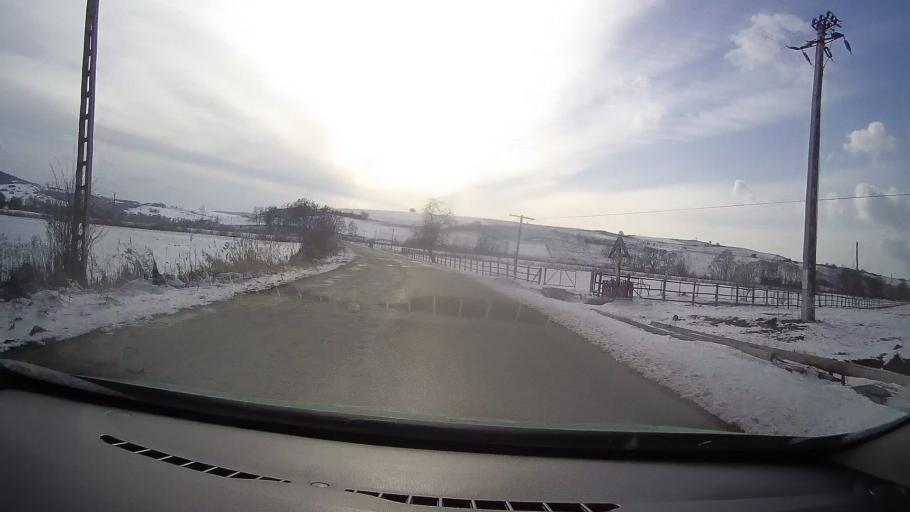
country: RO
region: Sibiu
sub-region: Comuna Iacobeni
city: Iacobeni
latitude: 46.0271
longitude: 24.7090
